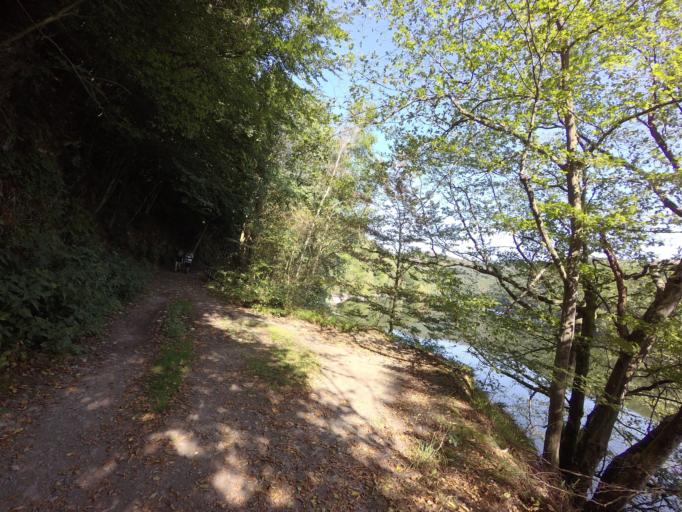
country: DE
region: North Rhine-Westphalia
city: Heimbach
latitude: 50.6002
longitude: 6.4124
